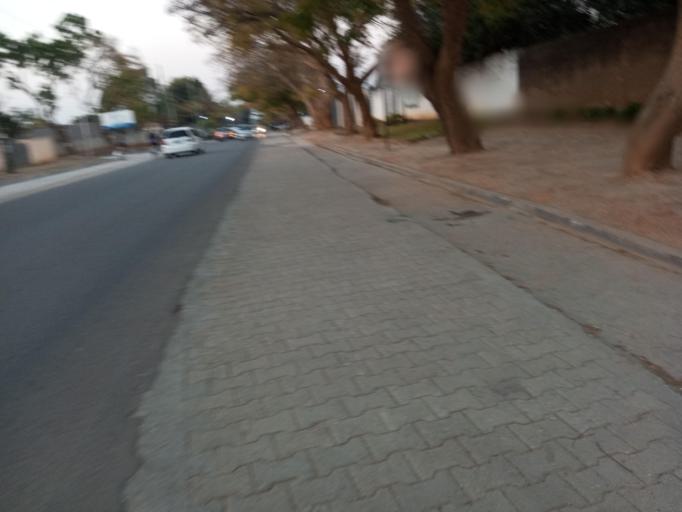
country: ZM
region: Lusaka
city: Lusaka
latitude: -15.4029
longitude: 28.2959
